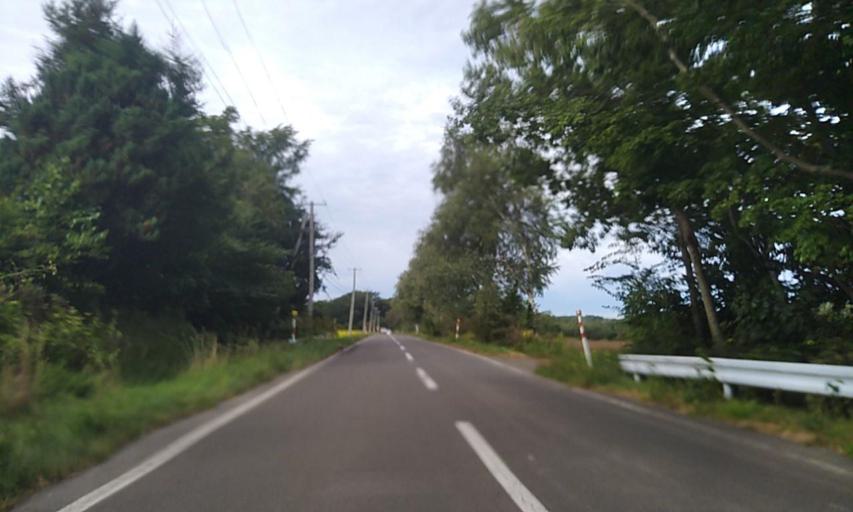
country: JP
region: Hokkaido
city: Abashiri
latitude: 43.7955
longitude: 144.5549
